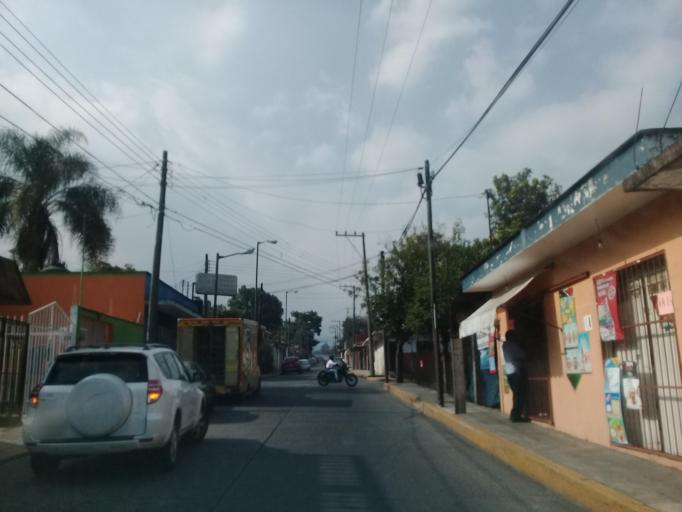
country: MX
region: Veracruz
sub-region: Ixhuatlancillo
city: Union y Progreso
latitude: 18.8666
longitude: -97.1079
